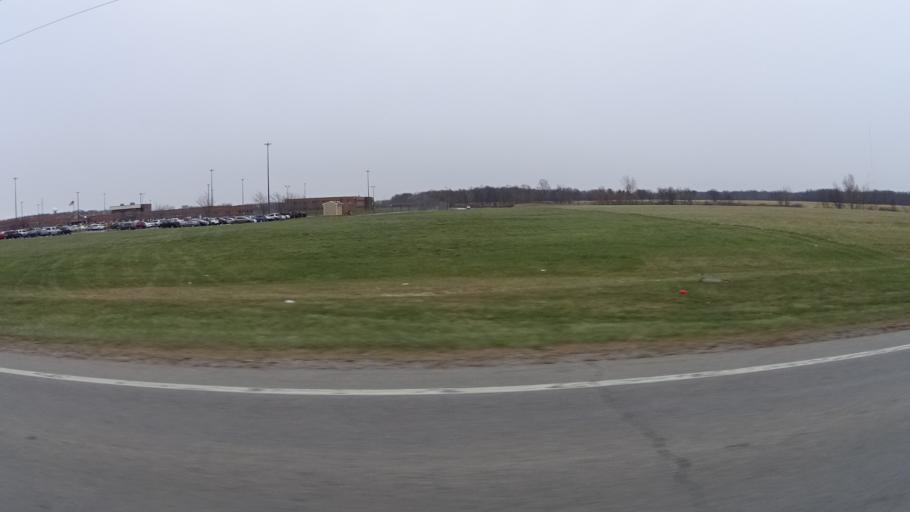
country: US
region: Ohio
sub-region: Lorain County
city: Eaton Estates
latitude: 41.2814
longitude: -82.0211
